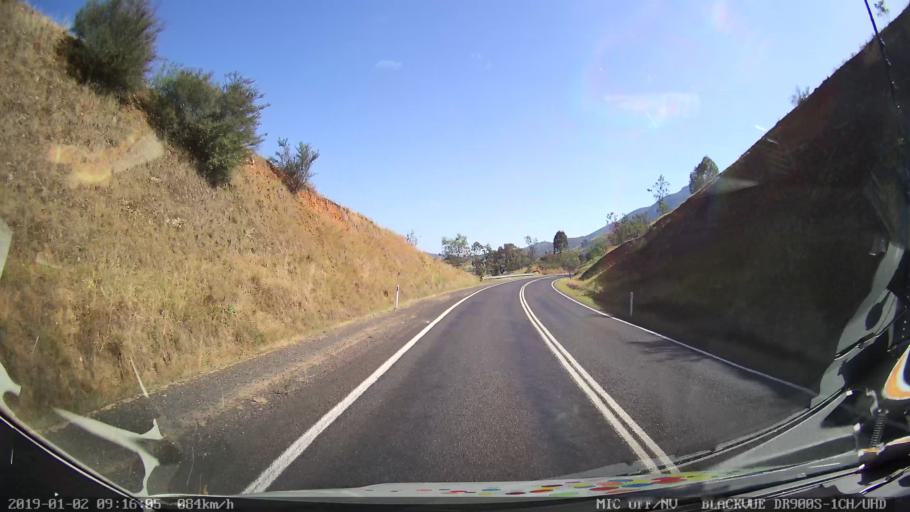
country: AU
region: New South Wales
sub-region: Tumut Shire
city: Tumut
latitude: -35.4573
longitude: 148.2818
